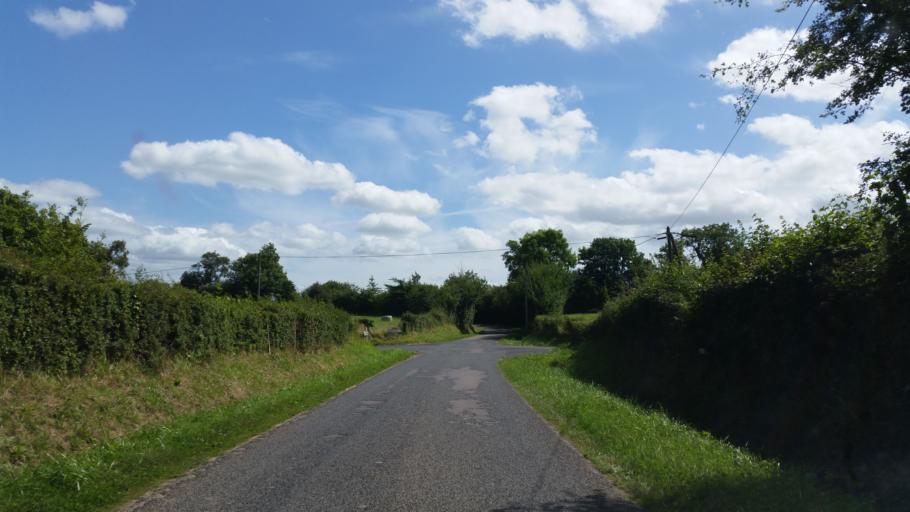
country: FR
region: Lower Normandy
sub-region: Departement de la Manche
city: Montebourg
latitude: 49.4629
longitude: -1.3319
